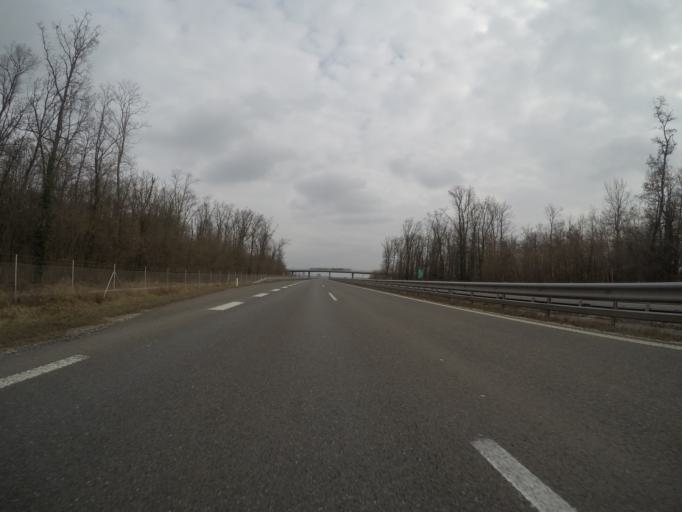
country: SI
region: Beltinci
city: Gancani
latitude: 46.6353
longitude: 16.2739
